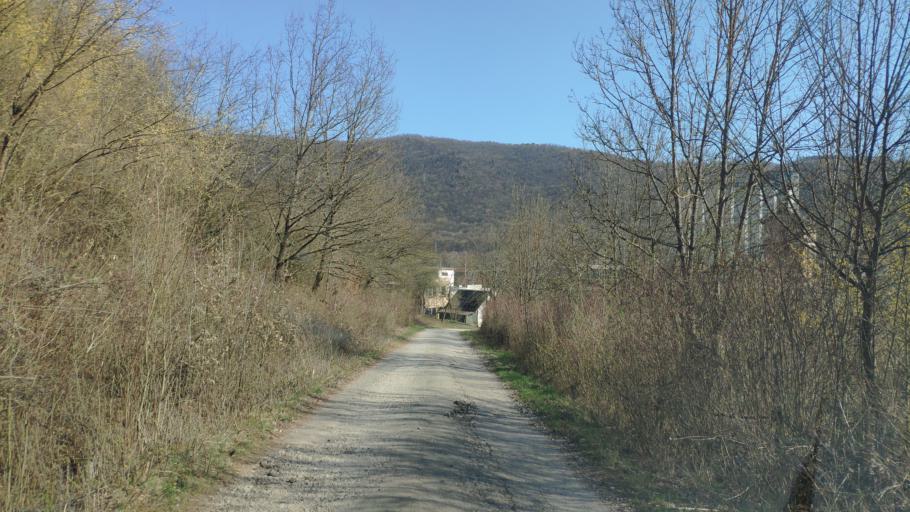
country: SK
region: Kosicky
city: Roznava
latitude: 48.5557
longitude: 20.4147
